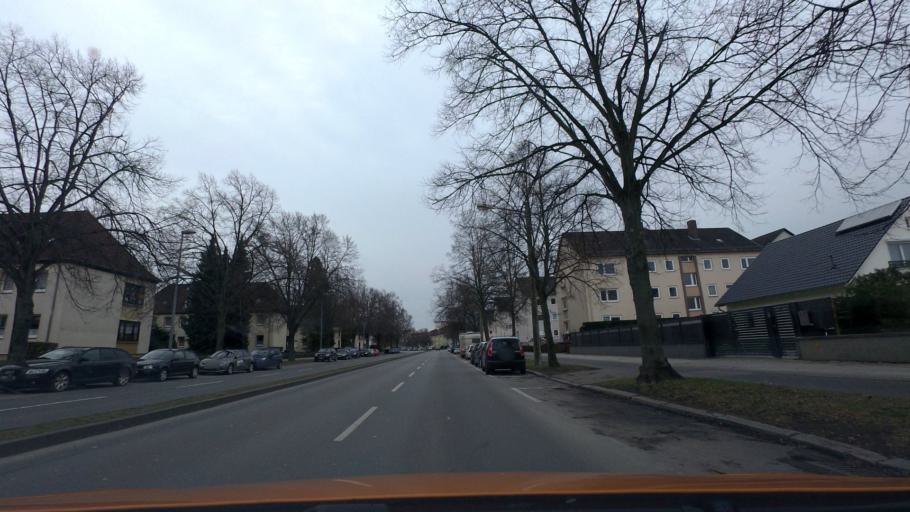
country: DE
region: Lower Saxony
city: Braunschweig
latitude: 52.2657
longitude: 10.5003
